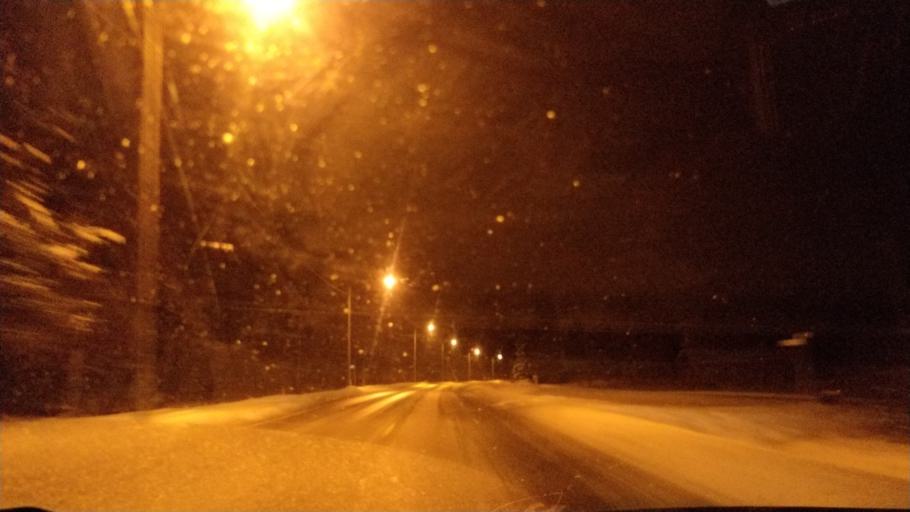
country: FI
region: Lapland
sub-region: Rovaniemi
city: Rovaniemi
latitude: 66.3121
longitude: 25.3618
